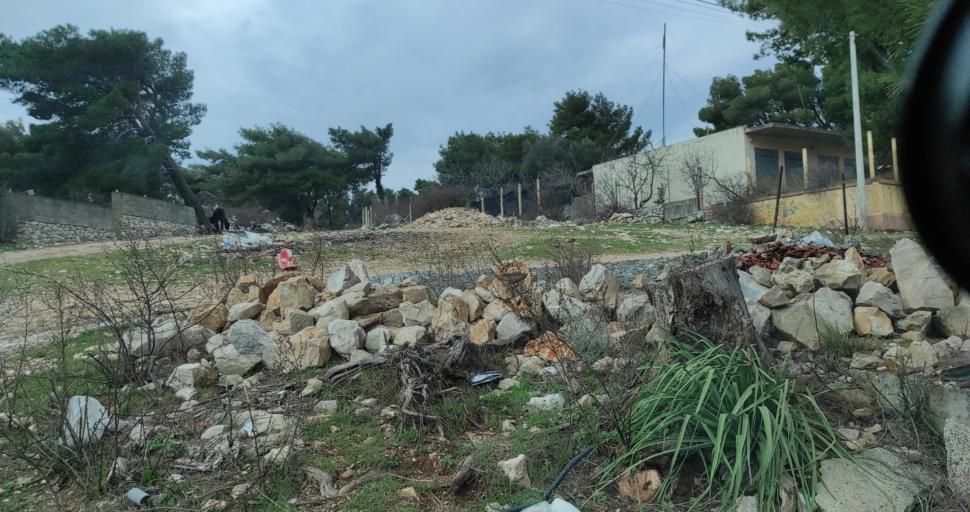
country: AL
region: Lezhe
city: Shengjin
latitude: 41.8142
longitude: 19.5832
